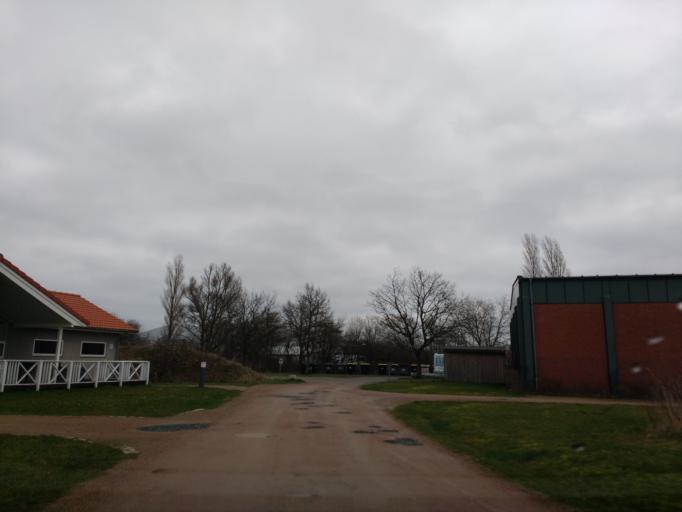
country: DE
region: Schleswig-Holstein
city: Grossenbrode
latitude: 54.3609
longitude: 11.0832
